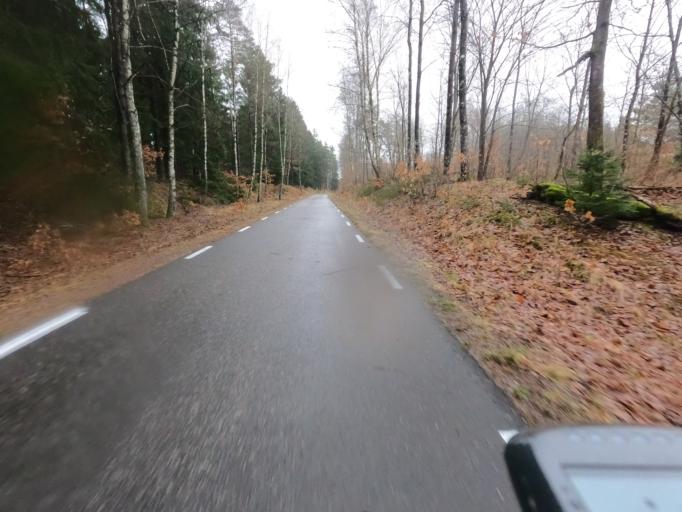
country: SE
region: Halland
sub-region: Halmstads Kommun
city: Aled
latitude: 56.7087
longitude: 13.0422
